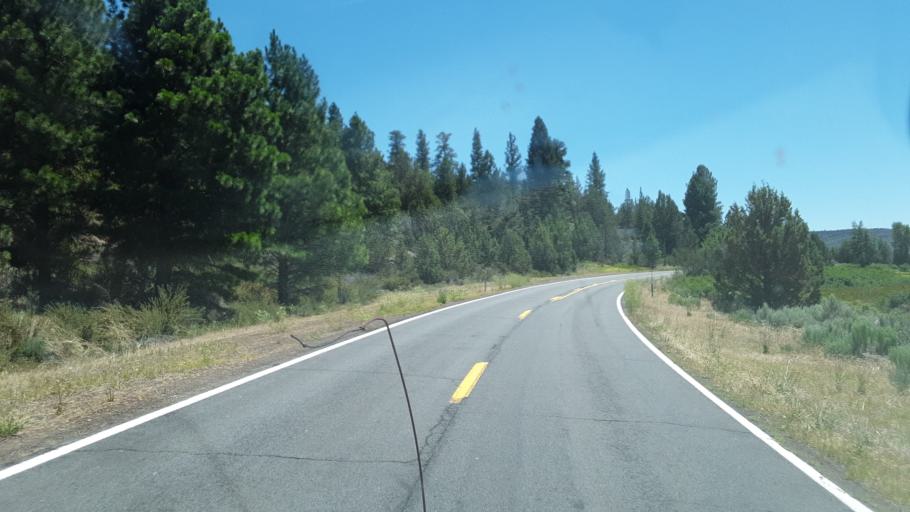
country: US
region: California
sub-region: Lassen County
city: Susanville
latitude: 40.6688
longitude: -120.6566
